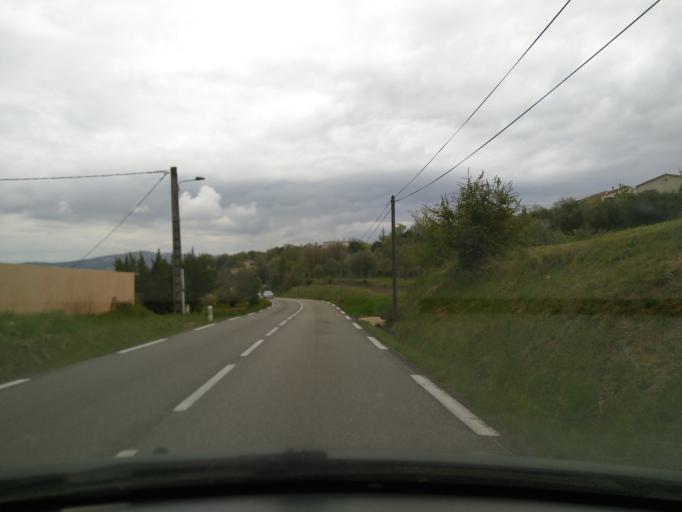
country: FR
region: Rhone-Alpes
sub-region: Departement de l'Ardeche
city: Ruoms
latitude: 44.3841
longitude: 4.3760
